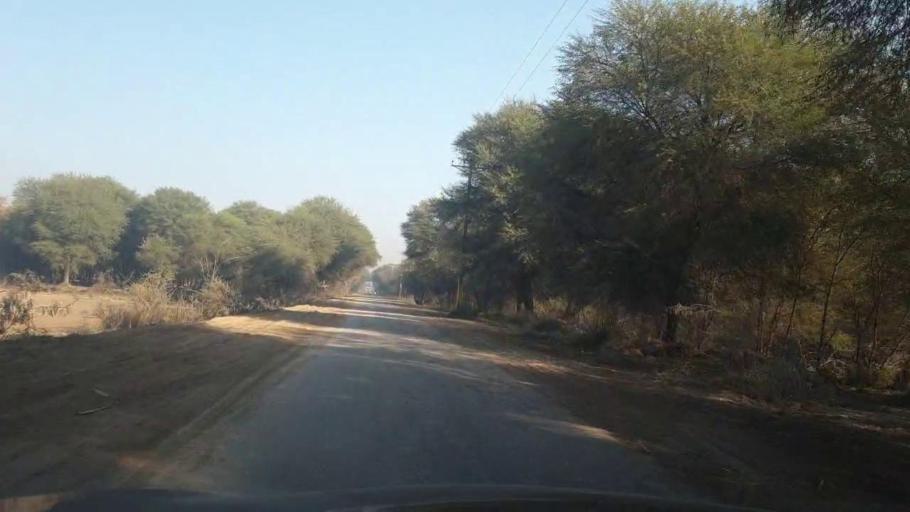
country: PK
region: Sindh
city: Mirpur Mathelo
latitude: 28.0609
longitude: 69.4639
